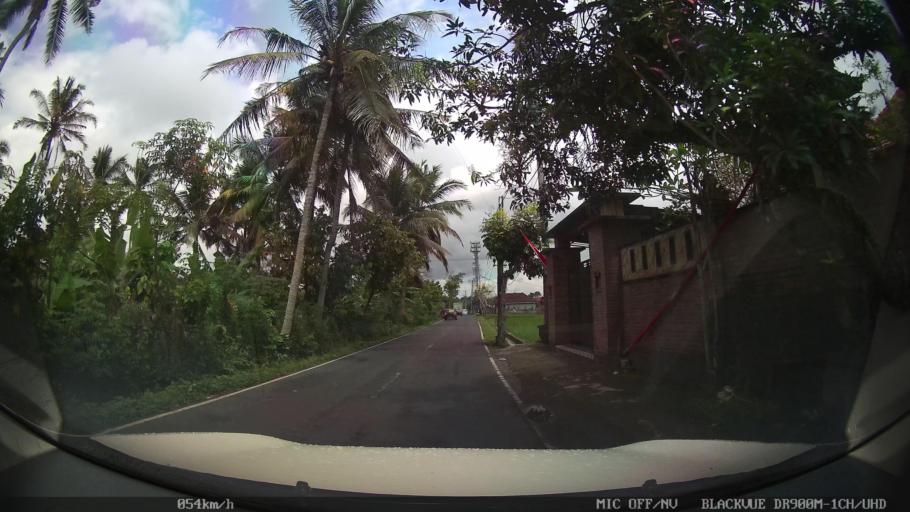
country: ID
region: Bali
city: Banjar Pekenjelodan
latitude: -8.5615
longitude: 115.1783
